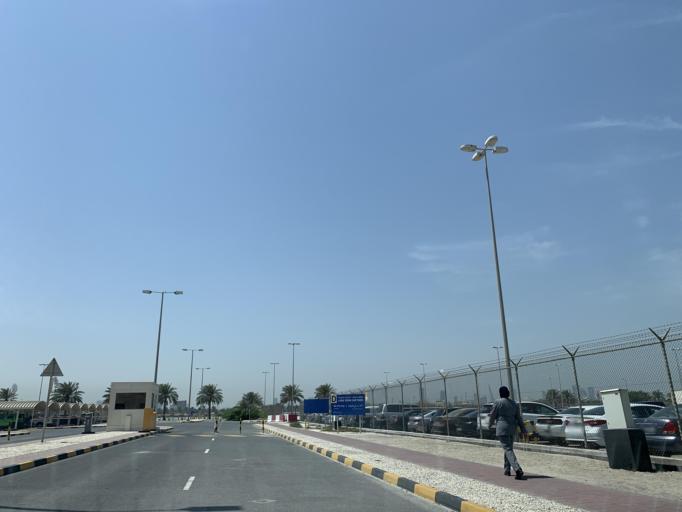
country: BH
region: Muharraq
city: Al Muharraq
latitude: 26.2645
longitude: 50.6290
